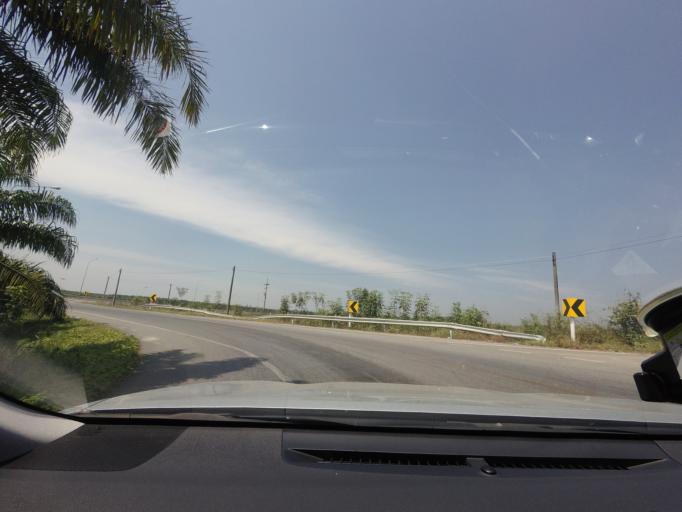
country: TH
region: Surat Thani
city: Tha Chang
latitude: 9.2191
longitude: 99.1811
